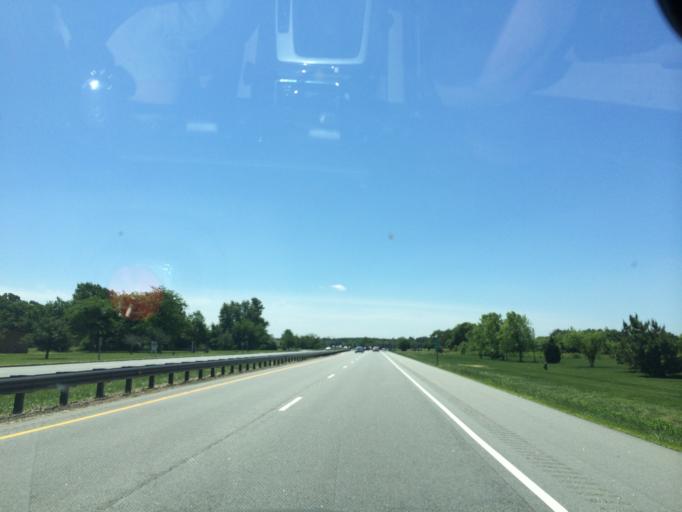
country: US
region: Maryland
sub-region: Talbot County
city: Easton
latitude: 38.7454
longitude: -76.0670
